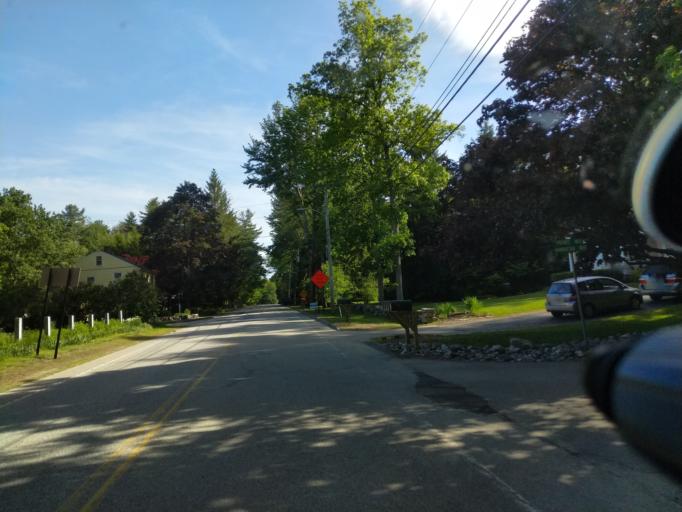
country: US
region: Maine
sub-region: Cumberland County
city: Falmouth
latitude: 43.7353
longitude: -70.3060
